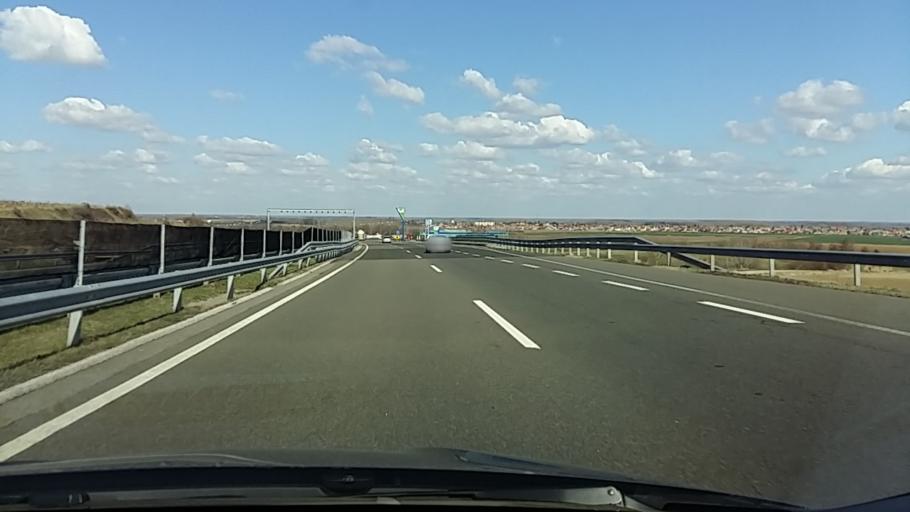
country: HU
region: Tolna
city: Bataszek
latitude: 46.1871
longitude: 18.6893
